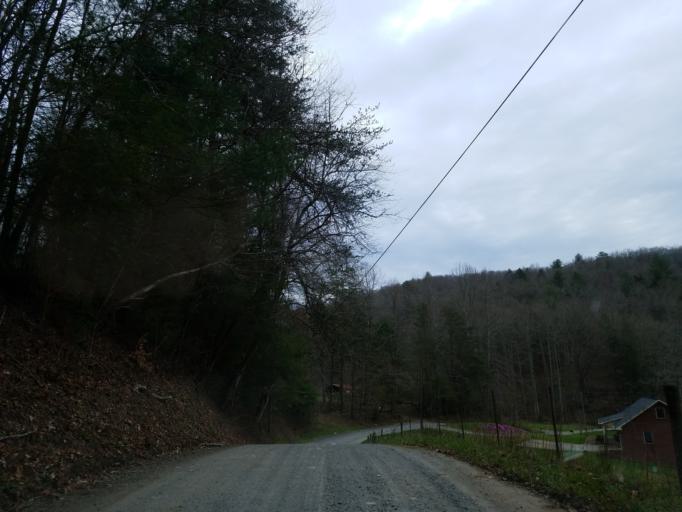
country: US
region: Georgia
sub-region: Fannin County
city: Blue Ridge
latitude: 34.7362
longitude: -84.2815
